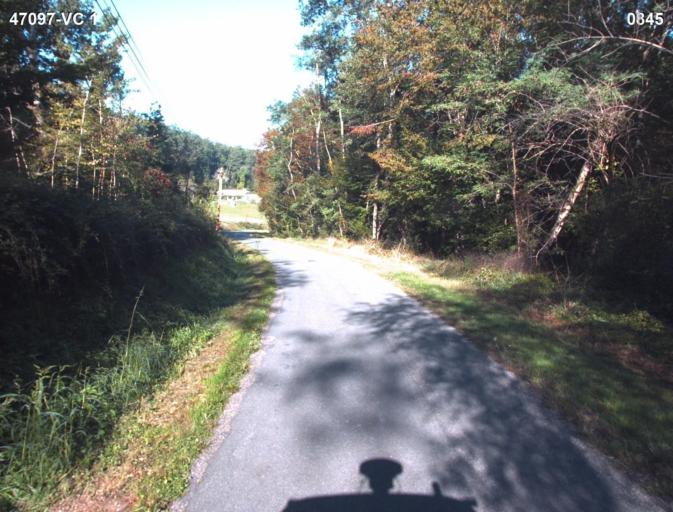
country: FR
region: Aquitaine
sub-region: Departement du Lot-et-Garonne
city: Vianne
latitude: 44.2153
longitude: 0.3505
